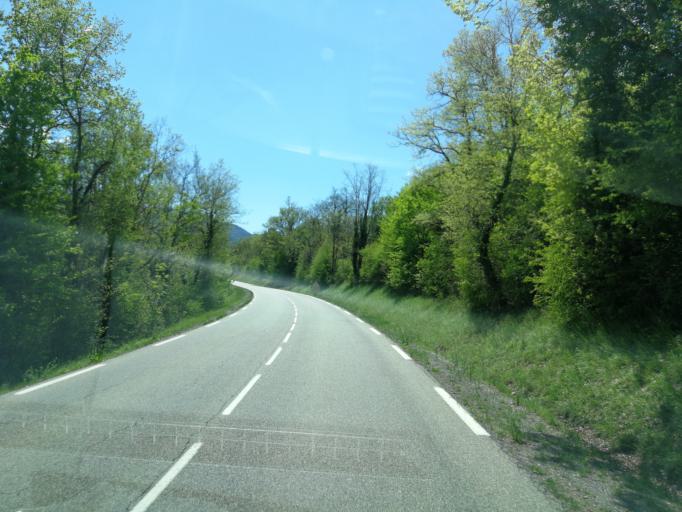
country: FR
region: Rhone-Alpes
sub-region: Departement de la Drome
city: Die
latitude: 44.7276
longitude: 5.2659
